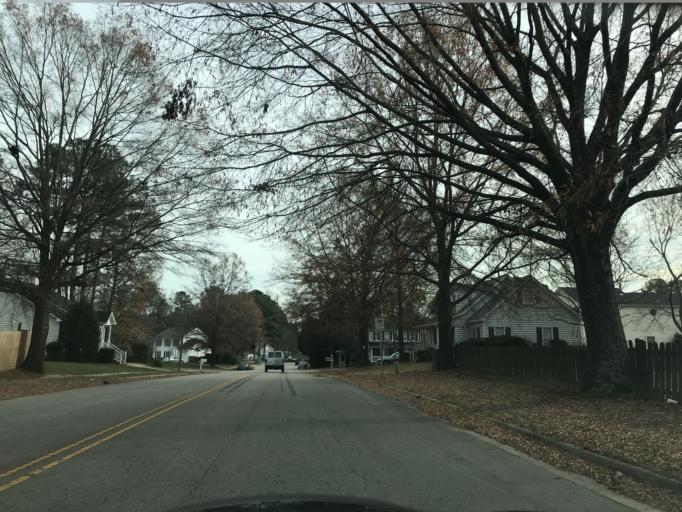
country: US
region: North Carolina
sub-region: Wake County
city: Knightdale
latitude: 35.8533
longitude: -78.5661
